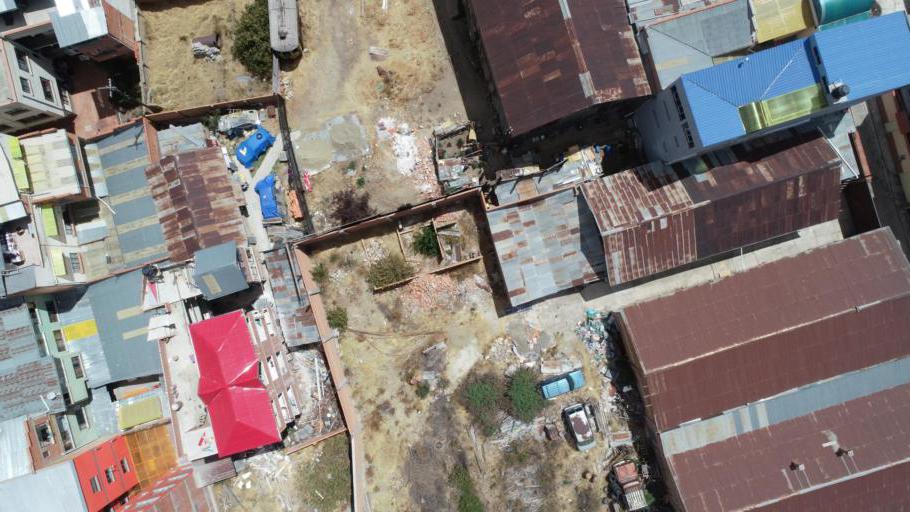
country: BO
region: La Paz
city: La Paz
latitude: -16.4810
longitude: -68.1494
